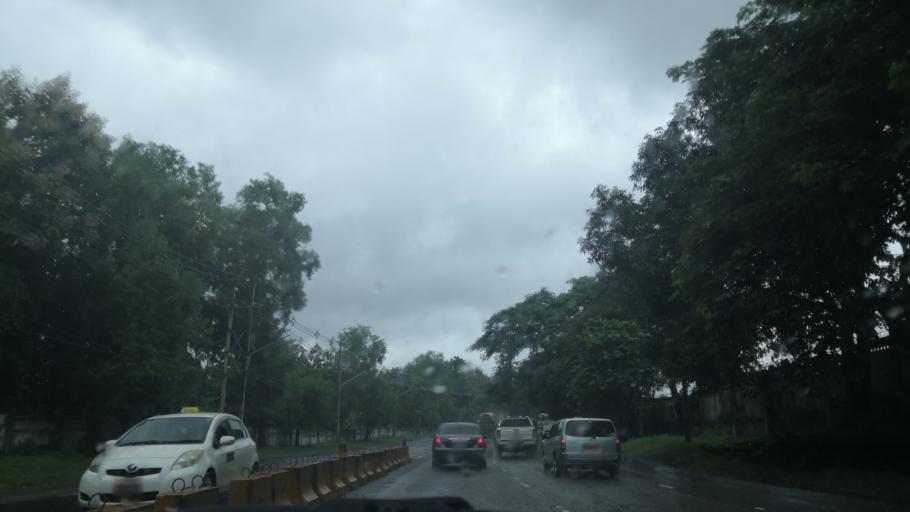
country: MM
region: Yangon
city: Yangon
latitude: 16.9066
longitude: 96.1291
